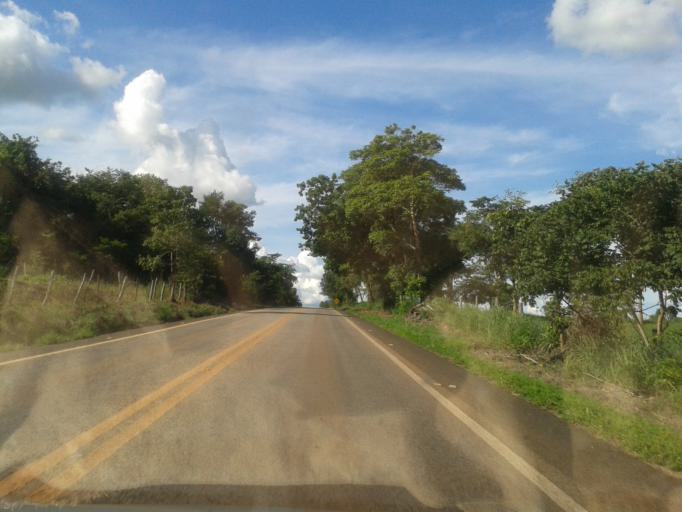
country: BR
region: Goias
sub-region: Mozarlandia
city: Mozarlandia
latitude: -14.6437
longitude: -50.5199
